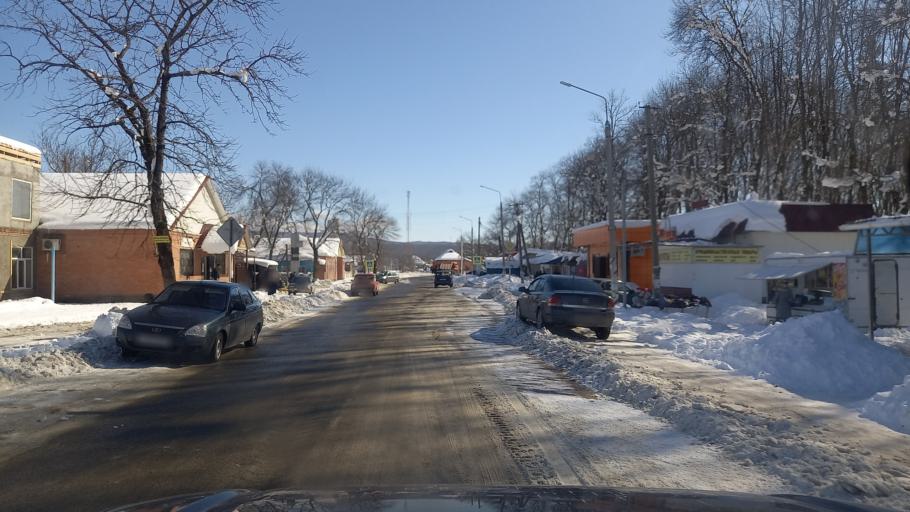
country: RU
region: Adygeya
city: Abadzekhskaya
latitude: 44.3917
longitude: 40.2193
